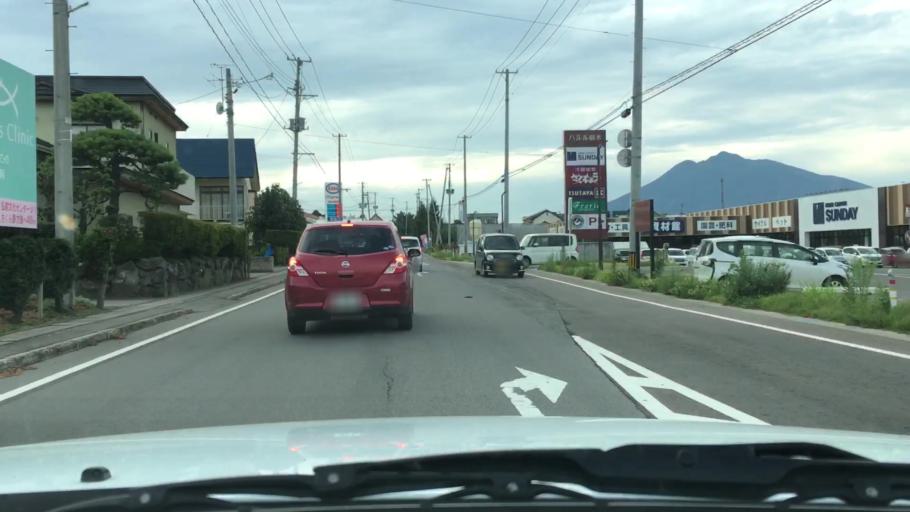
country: JP
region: Aomori
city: Hirosaki
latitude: 40.5870
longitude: 140.4601
